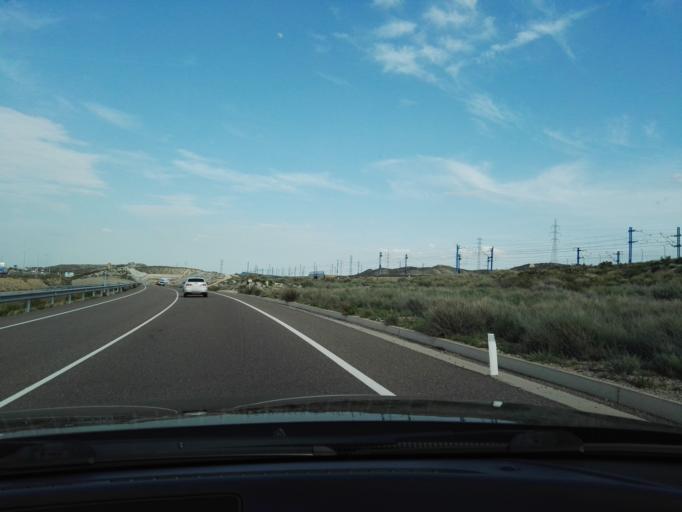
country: ES
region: Aragon
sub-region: Provincia de Zaragoza
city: Montecanal
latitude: 41.6187
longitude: -0.9678
